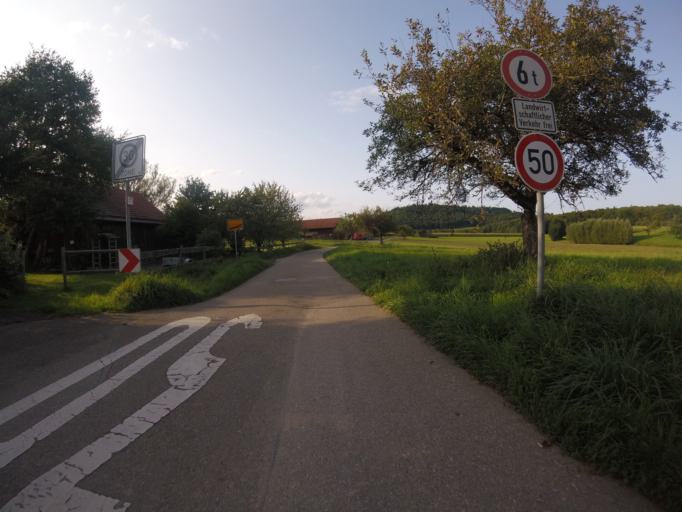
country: DE
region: Baden-Wuerttemberg
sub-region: Regierungsbezirk Stuttgart
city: Oppenweiler
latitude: 48.9741
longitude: 9.4340
